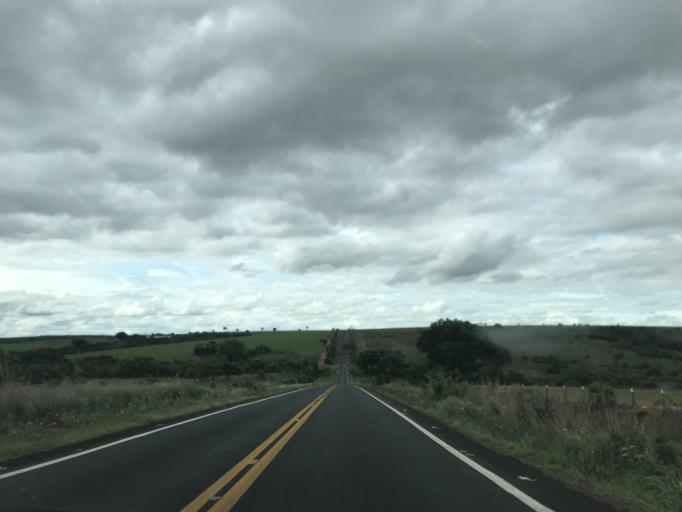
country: BR
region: Goias
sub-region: Caldas Novas
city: Caldas Novas
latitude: -17.5385
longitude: -48.7244
